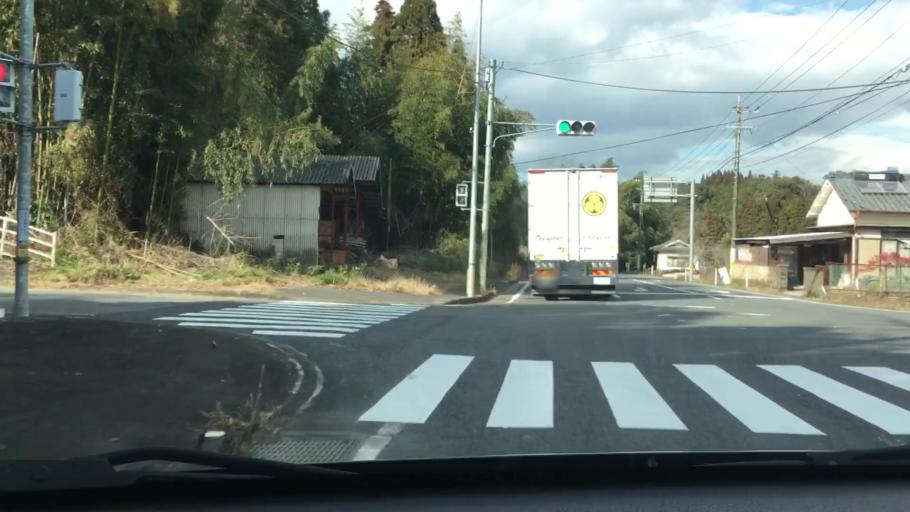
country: JP
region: Oita
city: Usuki
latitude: 33.0293
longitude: 131.6941
